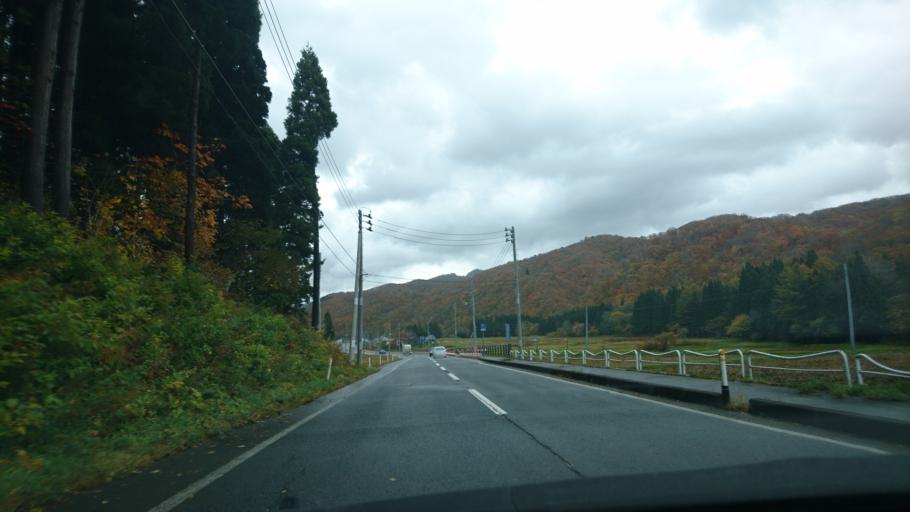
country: JP
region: Iwate
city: Shizukuishi
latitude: 39.5039
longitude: 140.8212
